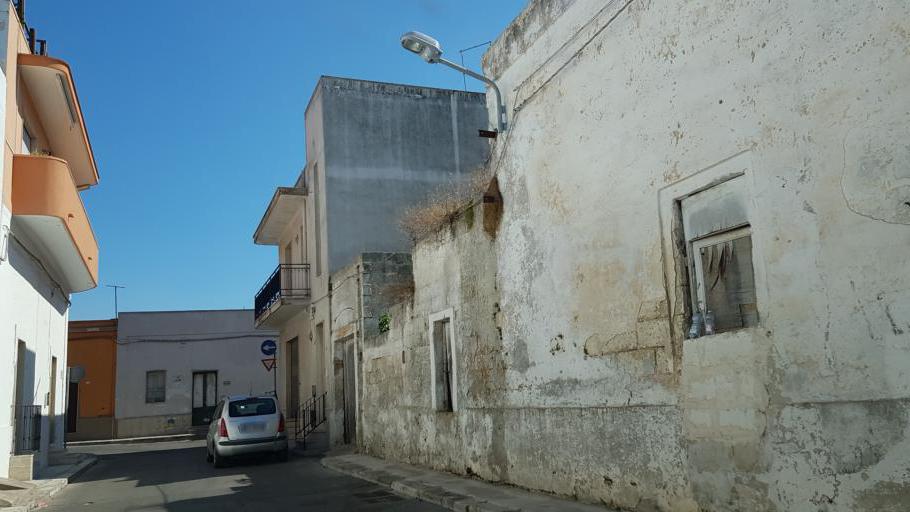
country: IT
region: Apulia
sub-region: Provincia di Brindisi
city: San Pancrazio Salentino
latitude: 40.4171
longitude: 17.8368
